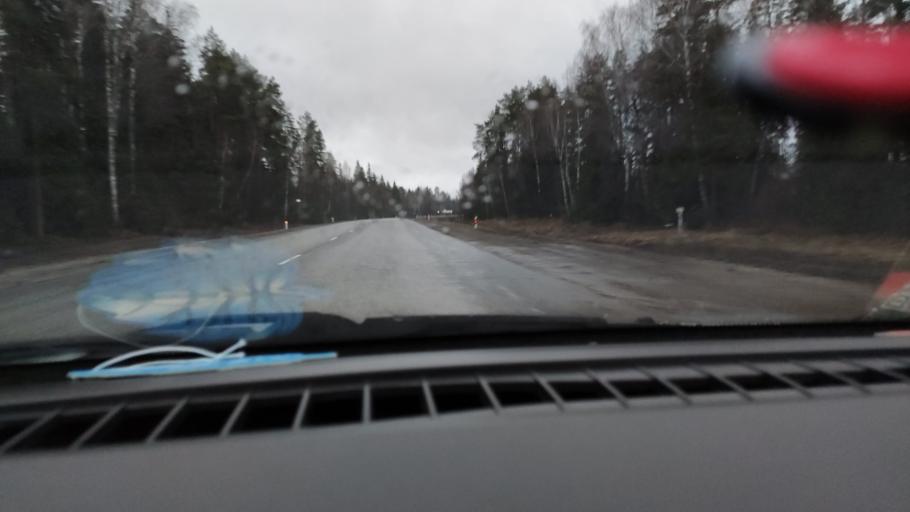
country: RU
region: Udmurtiya
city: Alnashi
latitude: 56.0922
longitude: 52.4467
